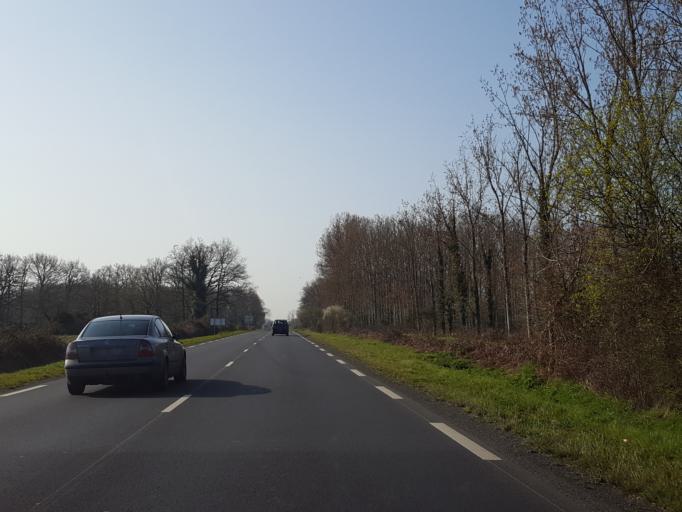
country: FR
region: Pays de la Loire
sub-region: Departement de la Loire-Atlantique
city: Geneston
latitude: 47.0443
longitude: -1.5084
